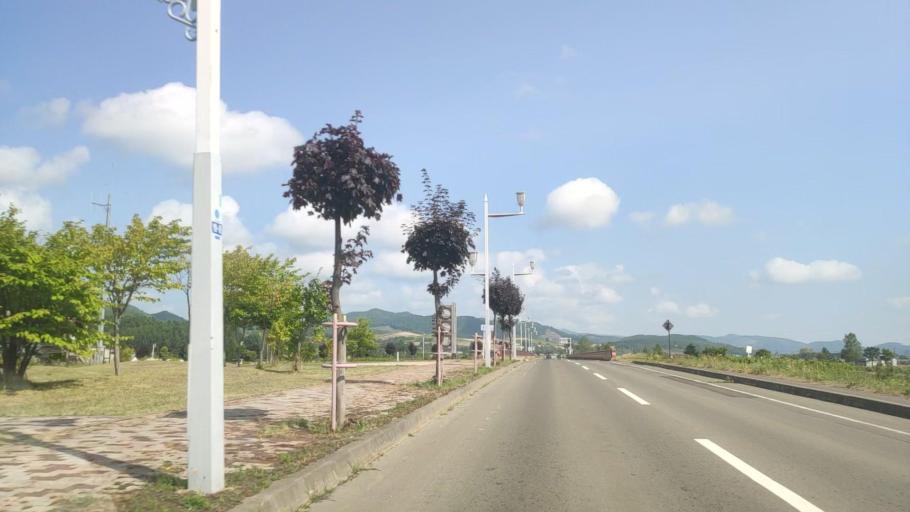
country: JP
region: Hokkaido
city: Shimo-furano
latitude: 43.3560
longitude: 142.3829
